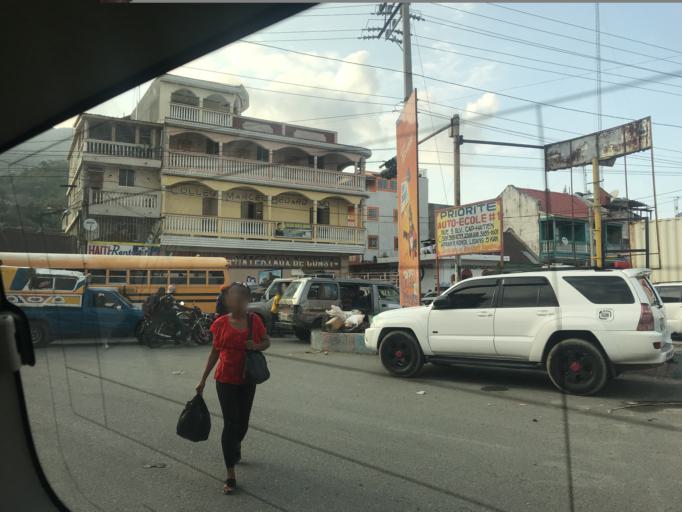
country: HT
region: Nord
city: Okap
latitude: 19.7554
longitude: -72.2020
